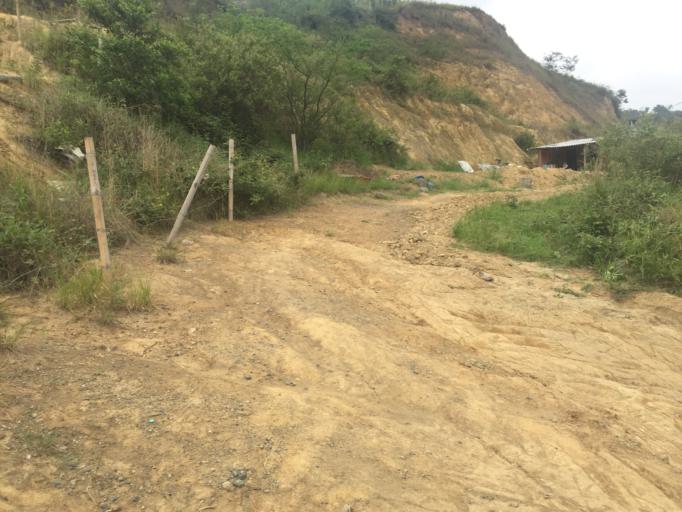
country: CO
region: Valle del Cauca
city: Cali
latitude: 3.4783
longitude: -76.5529
